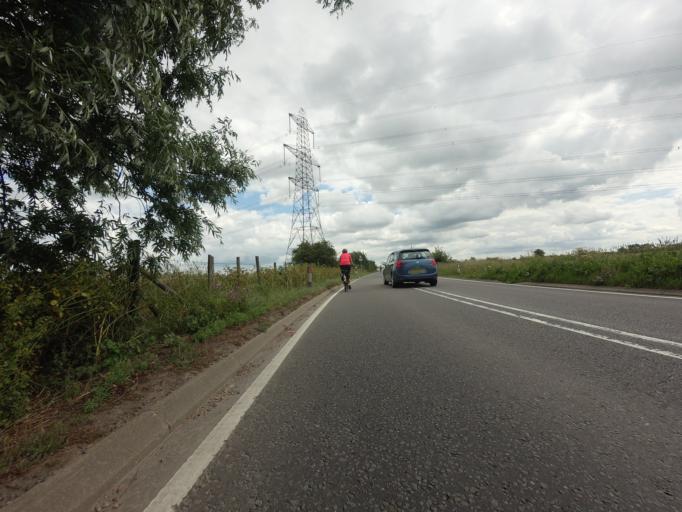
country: GB
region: England
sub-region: Medway
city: Allhallows
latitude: 51.4509
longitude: 0.6446
